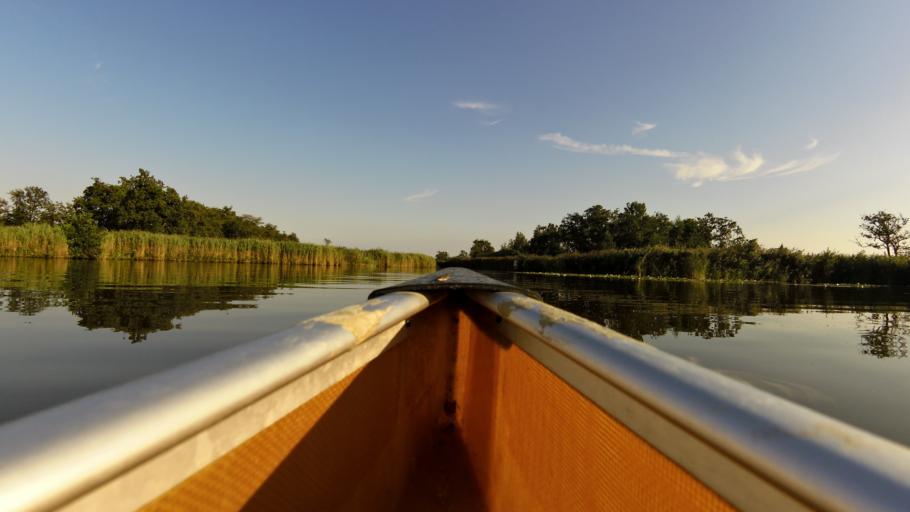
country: NL
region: South Holland
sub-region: Gemeente Nieuwkoop
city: Nieuwkoop
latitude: 52.1357
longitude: 4.7760
